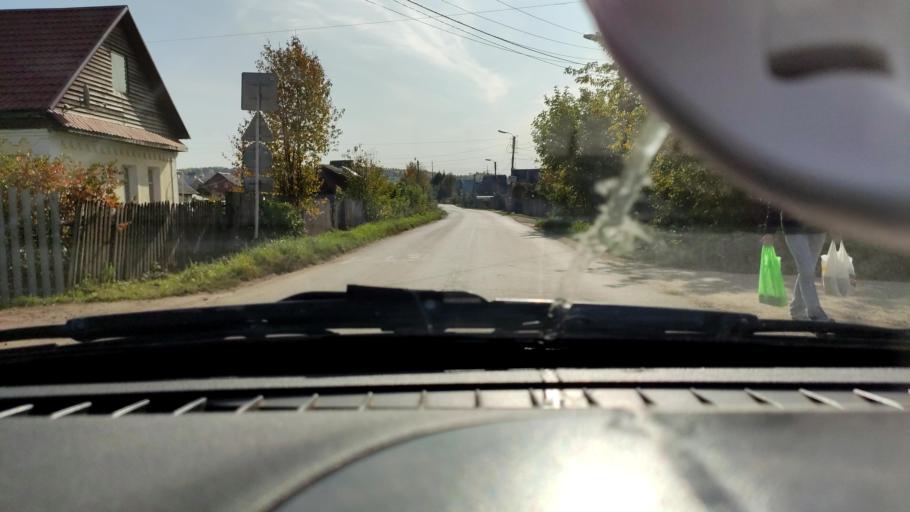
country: RU
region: Perm
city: Overyata
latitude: 58.0829
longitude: 55.8790
